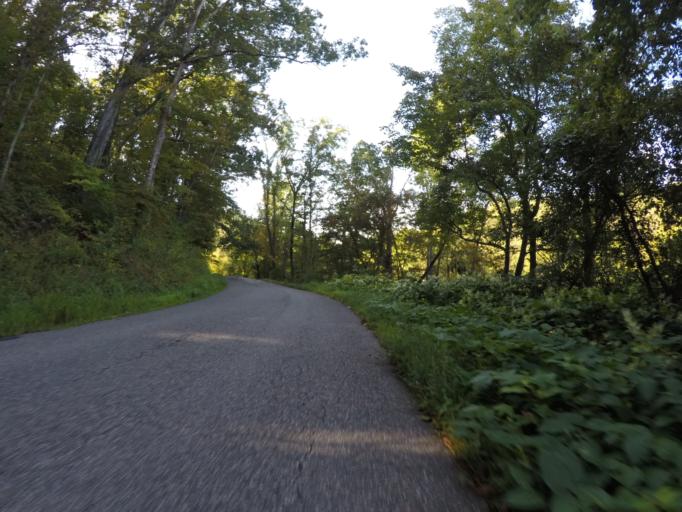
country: US
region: Kentucky
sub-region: Boyd County
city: Ashland
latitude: 38.5261
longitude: -82.5332
